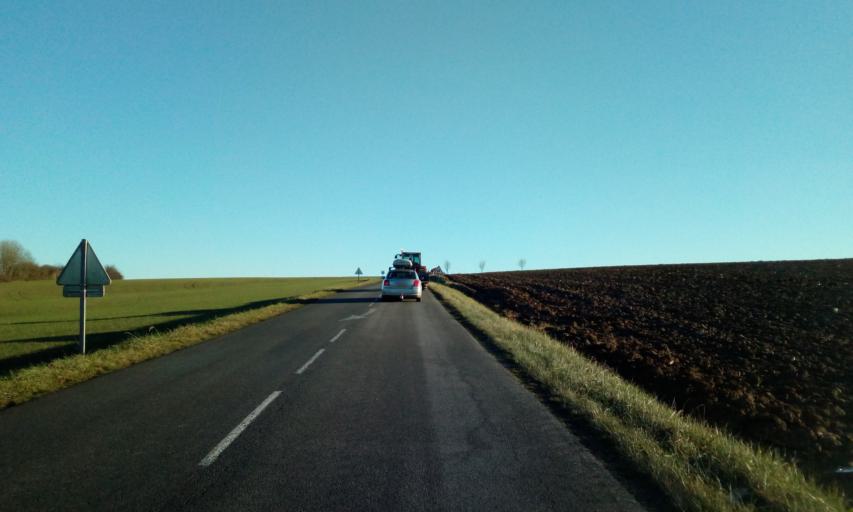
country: FR
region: Picardie
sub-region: Departement de l'Aisne
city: Rozoy-sur-Serre
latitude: 49.7025
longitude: 4.1572
